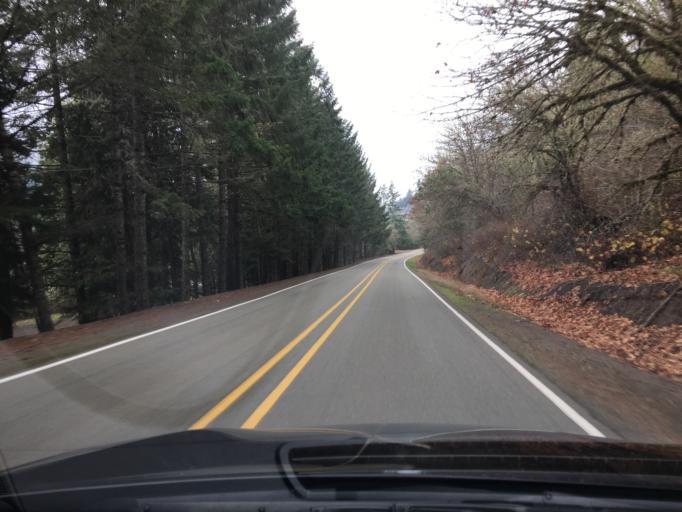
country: US
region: Oregon
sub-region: Douglas County
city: Sutherlin
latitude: 43.3838
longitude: -123.5260
